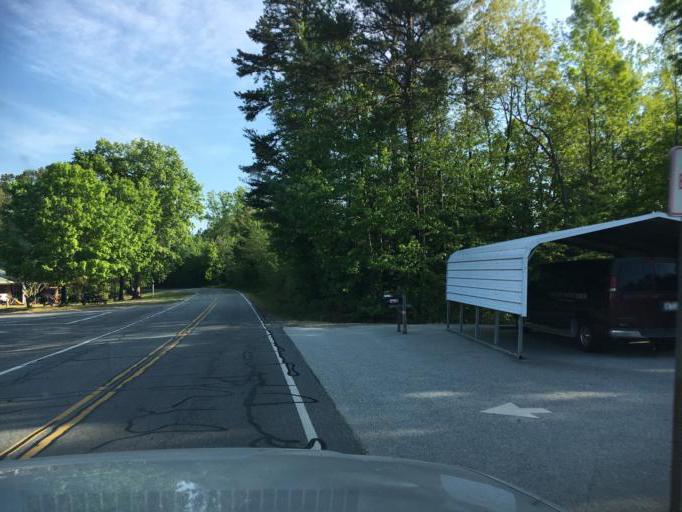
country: US
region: North Carolina
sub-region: Rutherford County
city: Rutherfordton
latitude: 35.3289
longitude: -81.9890
